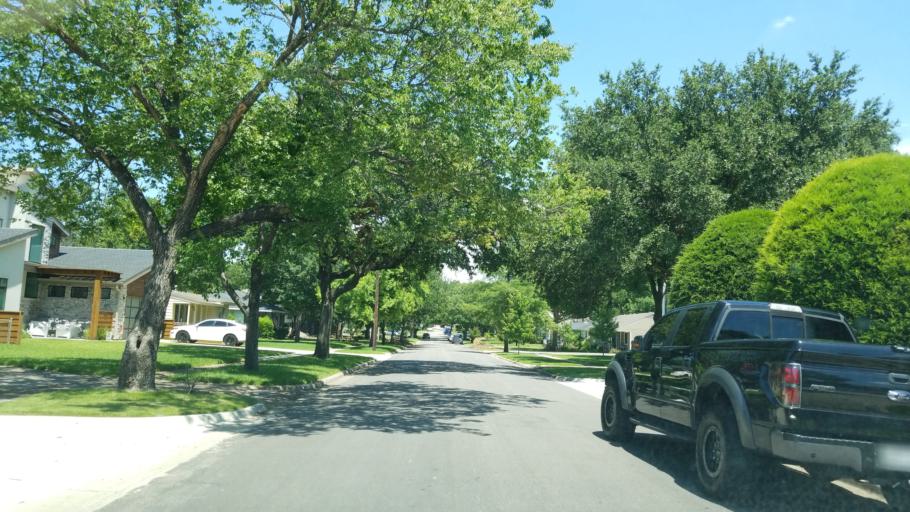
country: US
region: Texas
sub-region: Dallas County
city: University Park
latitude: 32.8753
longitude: -96.8485
